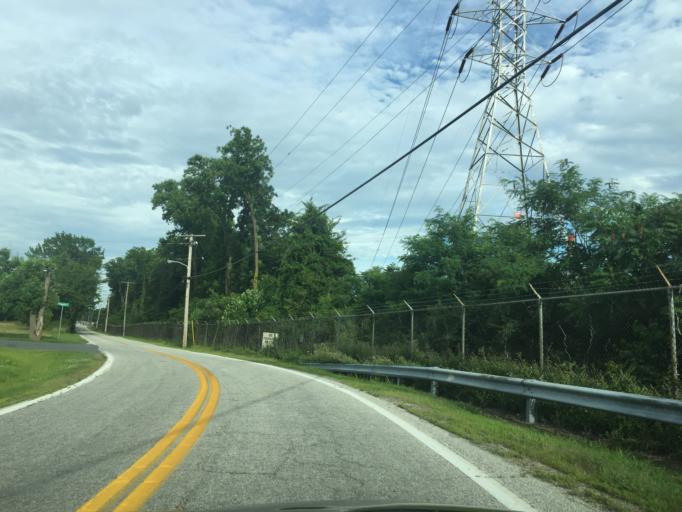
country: US
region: Maryland
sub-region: Baltimore County
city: Bowleys Quarters
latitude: 39.3279
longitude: -76.3693
